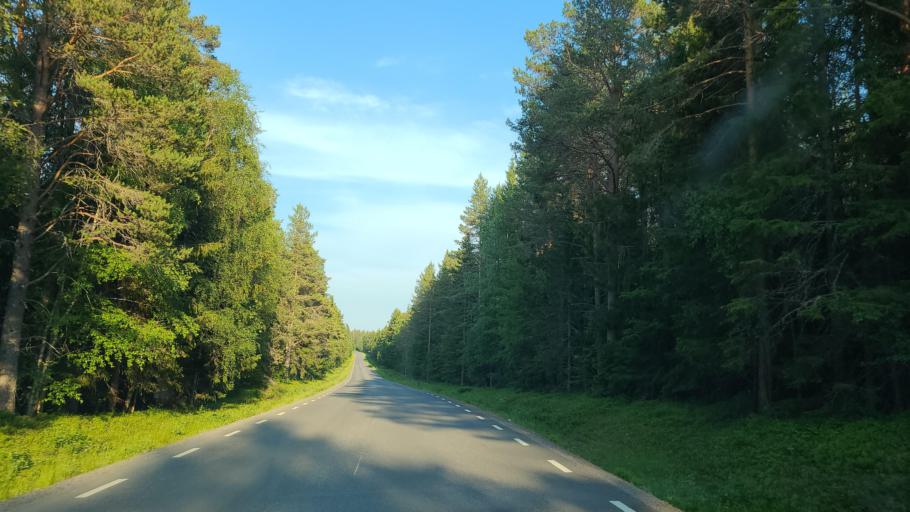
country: SE
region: Vaesterbotten
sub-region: Skelleftea Kommun
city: Burea
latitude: 64.4426
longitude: 21.4890
